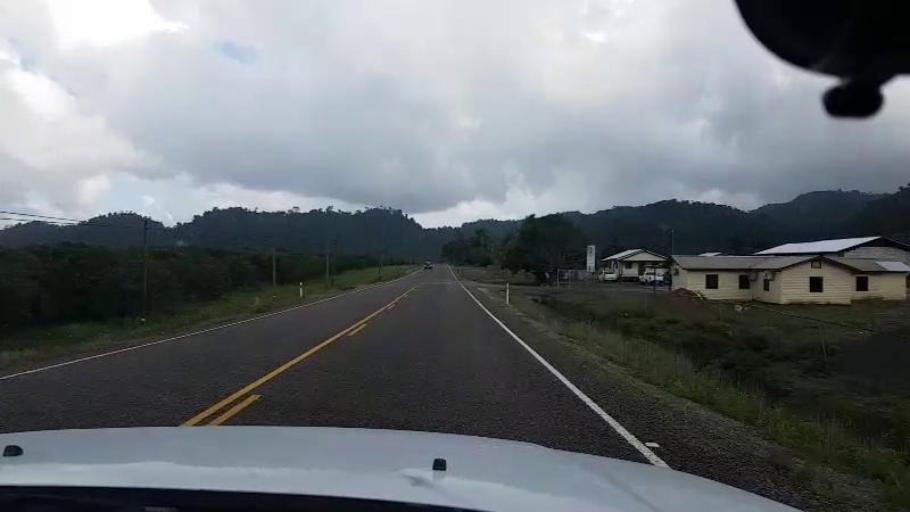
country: BZ
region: Cayo
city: Belmopan
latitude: 17.1484
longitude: -88.7081
